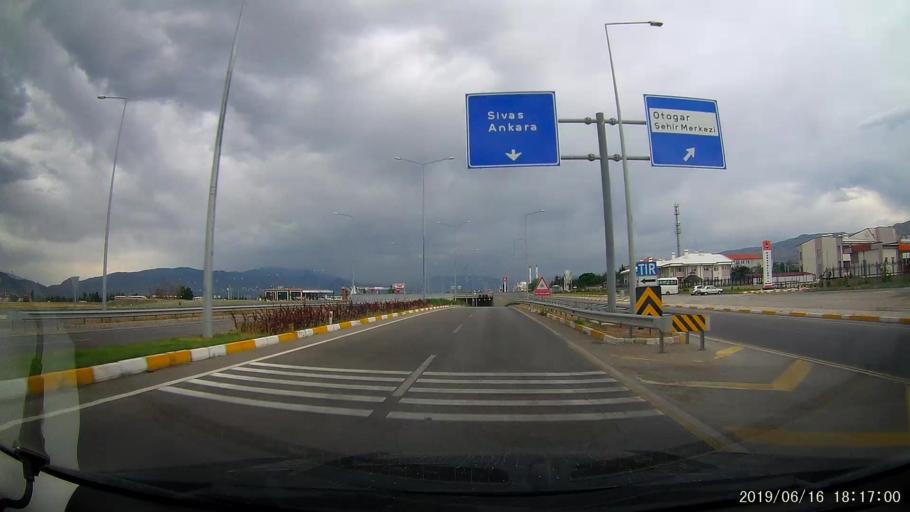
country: TR
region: Erzincan
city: Erzincan
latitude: 39.7319
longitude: 39.5393
